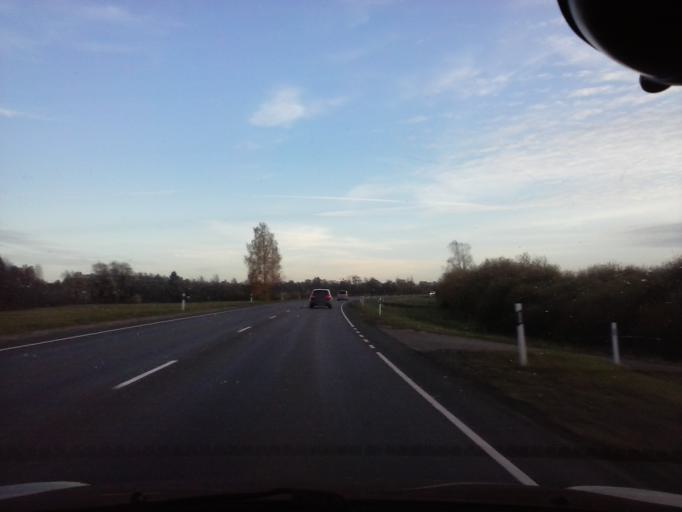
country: EE
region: Harju
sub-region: Nissi vald
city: Turba
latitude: 58.9240
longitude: 24.1114
